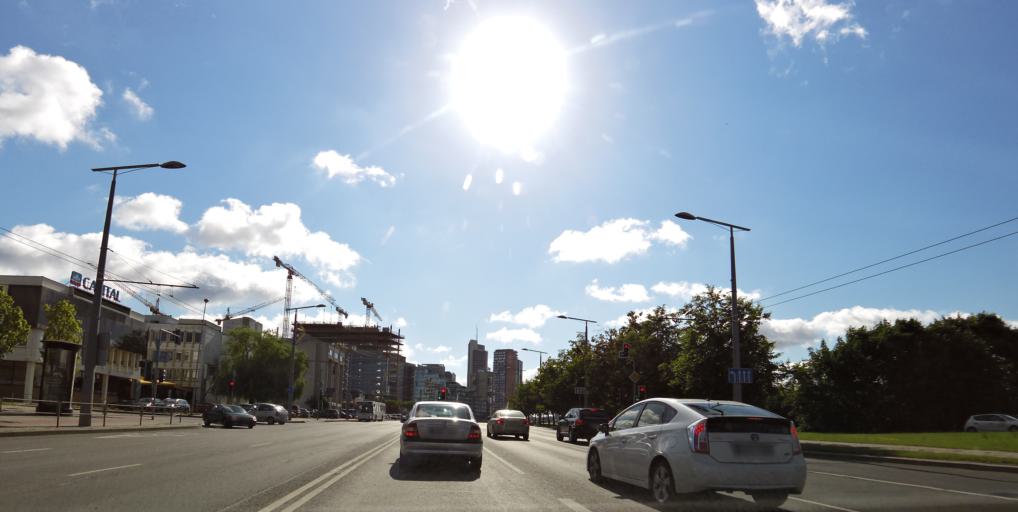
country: LT
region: Vilnius County
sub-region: Vilnius
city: Vilnius
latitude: 54.6983
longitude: 25.2670
